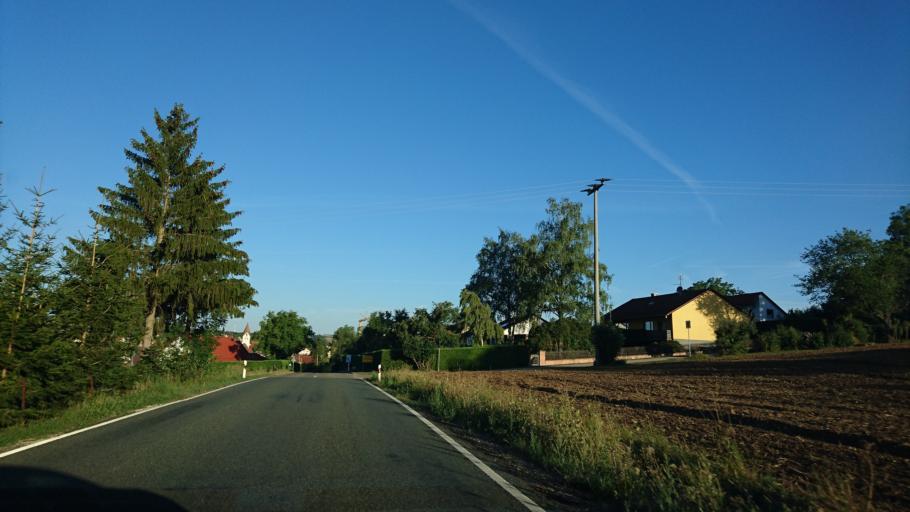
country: DE
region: Bavaria
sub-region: Regierungsbezirk Mittelfranken
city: Nennslingen
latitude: 49.0473
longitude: 11.1401
